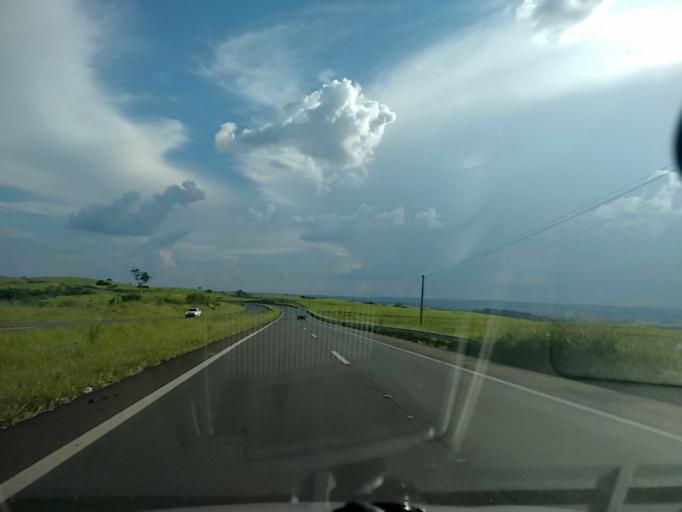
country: BR
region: Sao Paulo
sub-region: Duartina
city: Duartina
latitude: -22.2917
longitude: -49.4950
